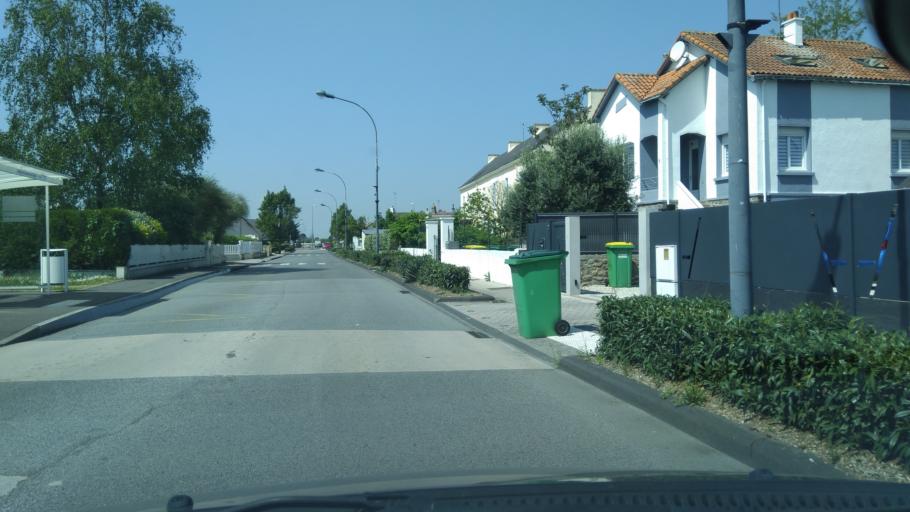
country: FR
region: Pays de la Loire
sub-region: Departement de la Loire-Atlantique
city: Montoir-de-Bretagne
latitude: 47.3267
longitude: -2.1563
